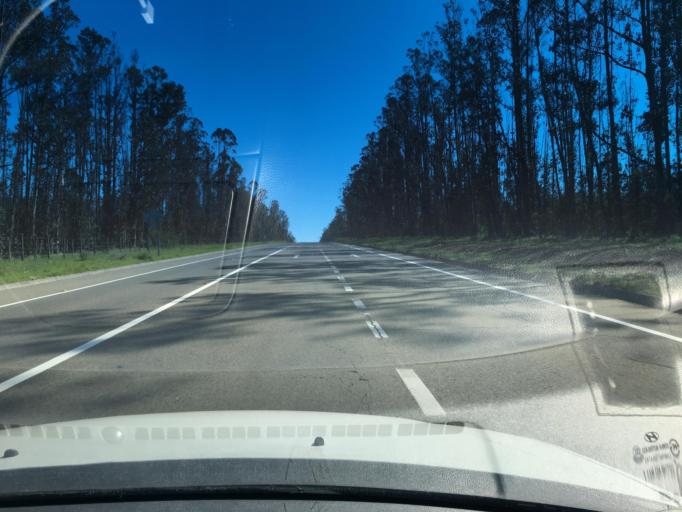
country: CL
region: Valparaiso
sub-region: San Antonio Province
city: El Tabo
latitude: -33.4078
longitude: -71.5559
